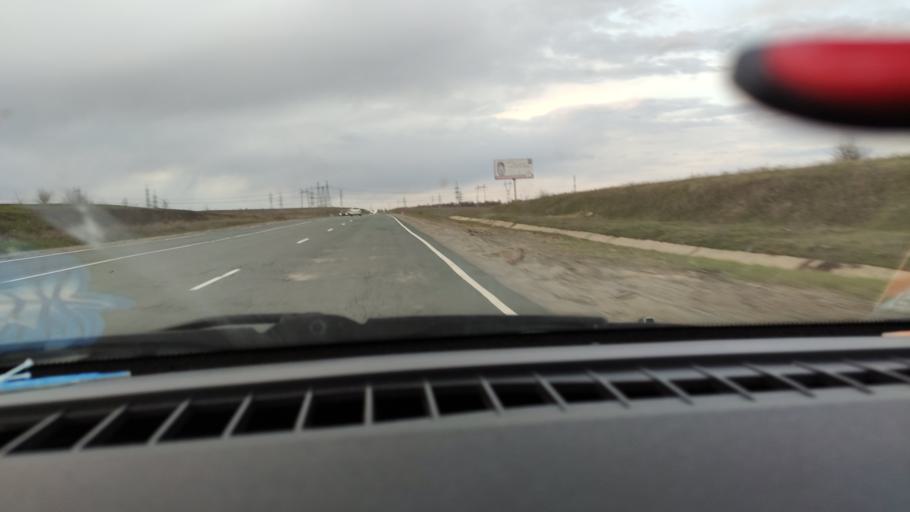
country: RU
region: Saratov
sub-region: Saratovskiy Rayon
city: Saratov
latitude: 51.7646
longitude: 46.0760
